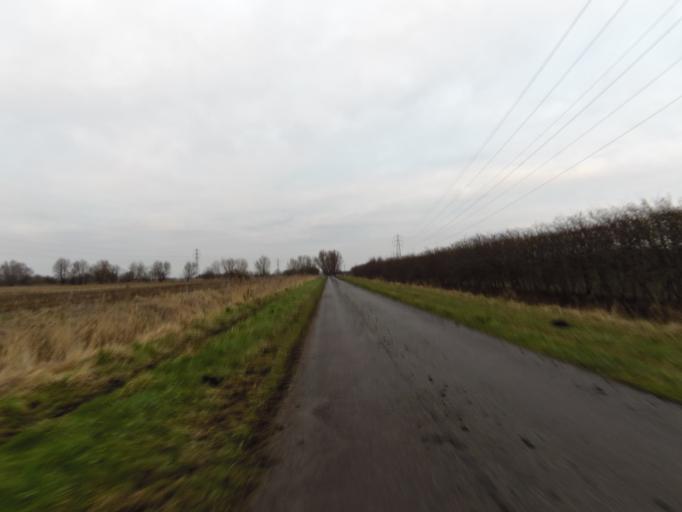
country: GB
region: England
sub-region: Cambridgeshire
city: Bottisham
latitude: 52.2565
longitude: 0.2379
